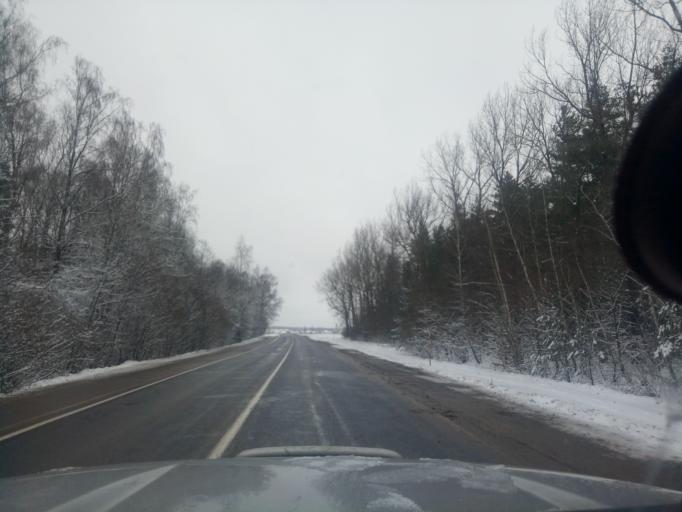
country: BY
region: Minsk
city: Kapyl'
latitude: 53.1286
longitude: 27.0801
